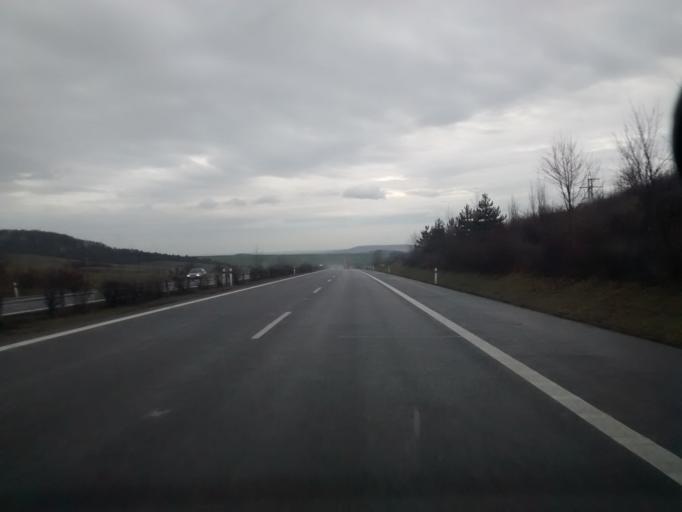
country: CZ
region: Central Bohemia
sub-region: Okres Melnik
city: Veltrusy
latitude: 50.3274
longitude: 14.2958
